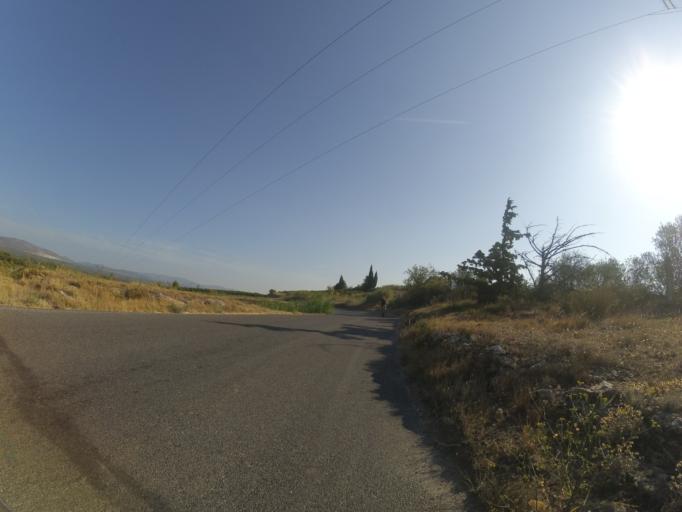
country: FR
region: Languedoc-Roussillon
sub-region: Departement des Pyrenees-Orientales
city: Baixas
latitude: 42.7660
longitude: 2.8264
